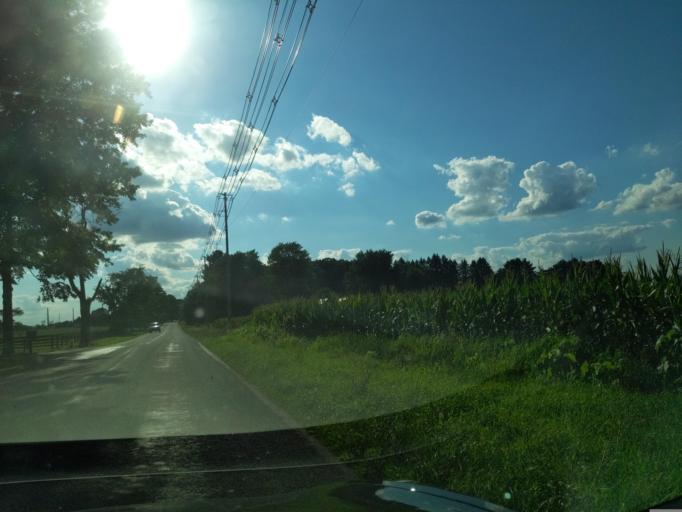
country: US
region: Michigan
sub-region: Ingham County
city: Mason
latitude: 42.5749
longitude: -84.4643
